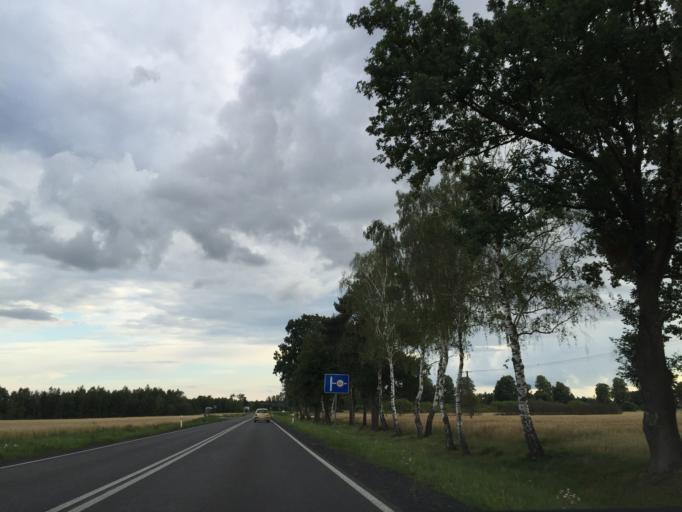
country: PL
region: Lublin Voivodeship
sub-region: Powiat radzynski
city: Borki
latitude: 51.6787
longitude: 22.4874
